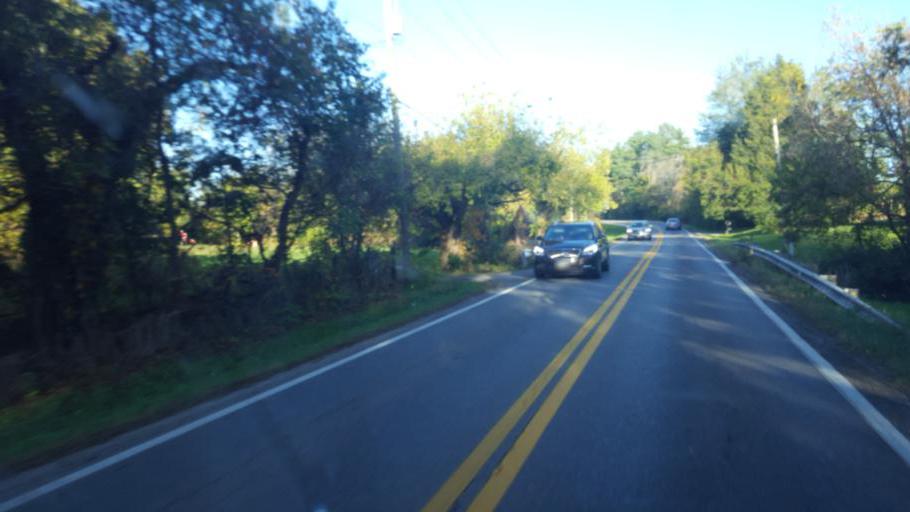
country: US
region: Ohio
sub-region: Franklin County
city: New Albany
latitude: 40.0191
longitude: -82.8082
